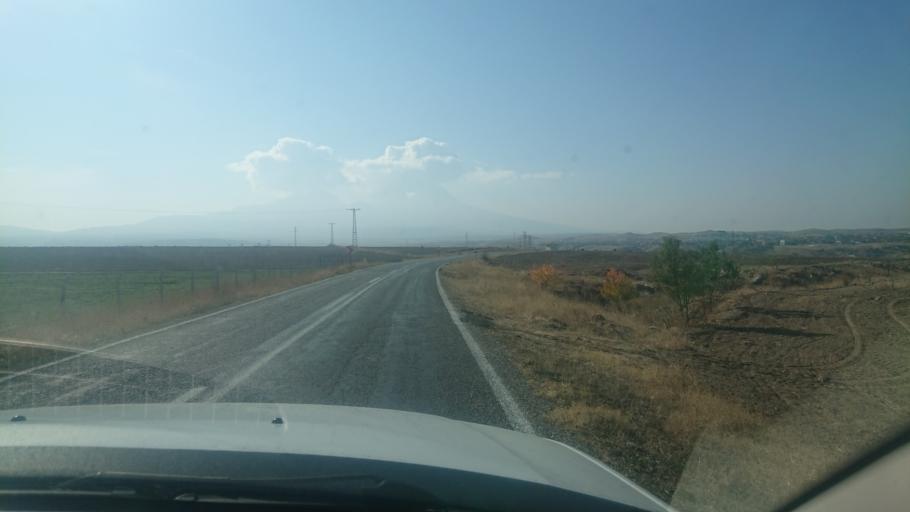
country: TR
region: Aksaray
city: Guzelyurt
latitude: 38.2461
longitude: 34.3239
